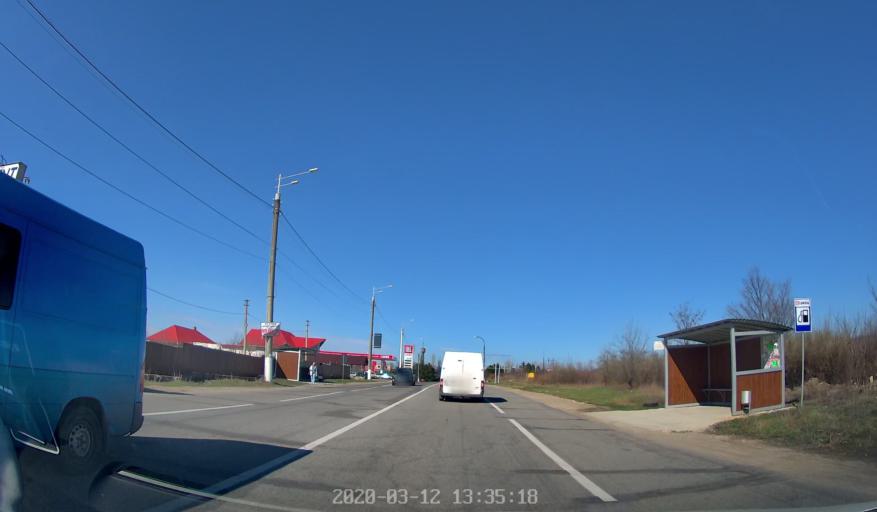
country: MD
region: Laloveni
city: Ialoveni
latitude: 46.9705
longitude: 28.7662
